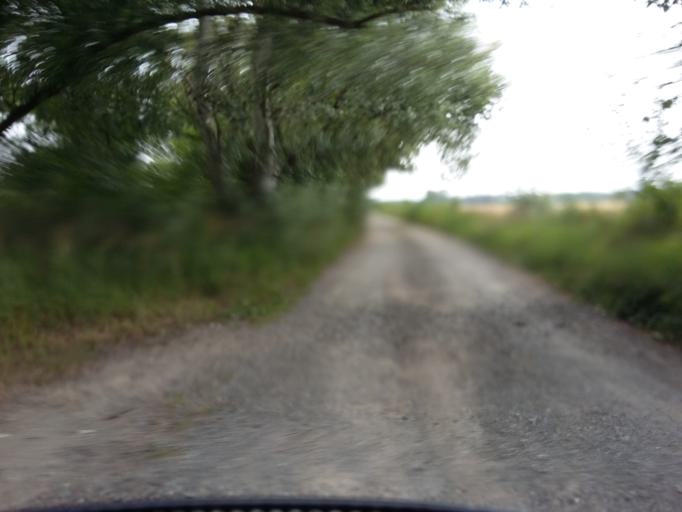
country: AT
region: Lower Austria
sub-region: Politischer Bezirk Ganserndorf
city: Drosing
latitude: 48.4947
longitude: 16.9474
